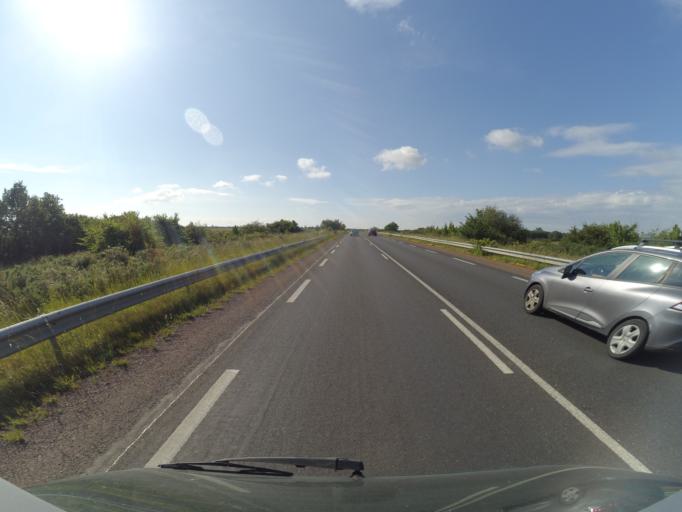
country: FR
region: Poitou-Charentes
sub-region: Departement de la Charente-Maritime
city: Saint-Agnant
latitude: 45.8547
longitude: -0.9621
